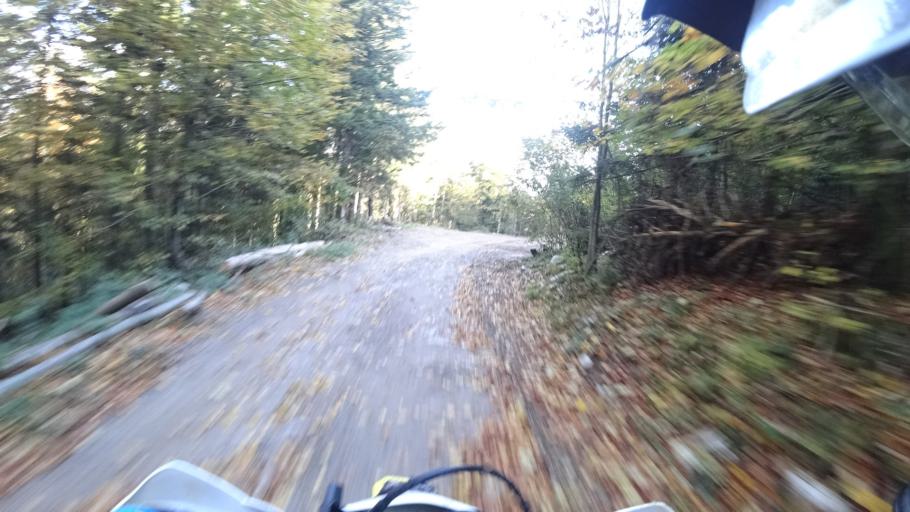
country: HR
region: Karlovacka
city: Plaski
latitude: 45.0352
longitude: 15.3747
